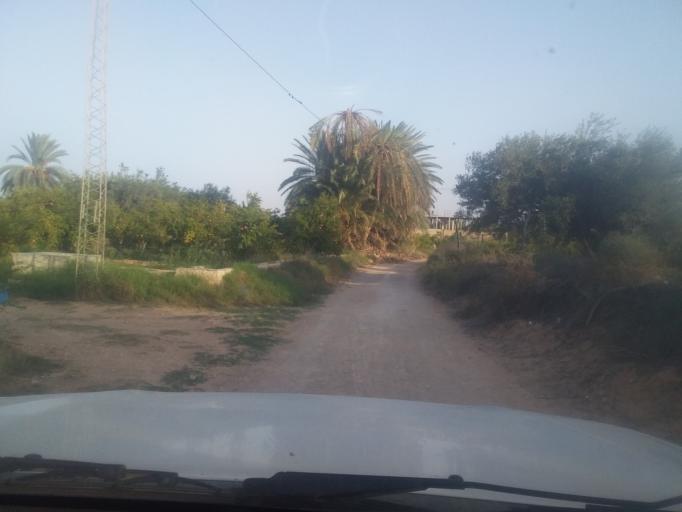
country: TN
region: Qabis
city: Gabes
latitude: 33.6310
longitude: 10.2947
